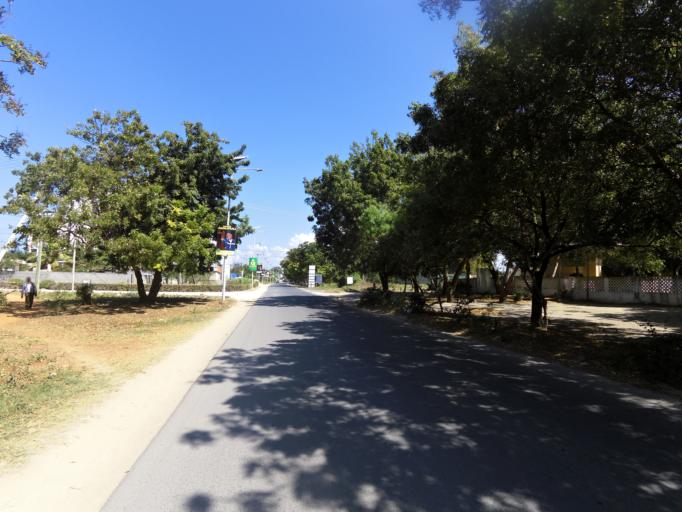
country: TZ
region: Dar es Salaam
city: Magomeni
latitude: -6.7455
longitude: 39.2828
